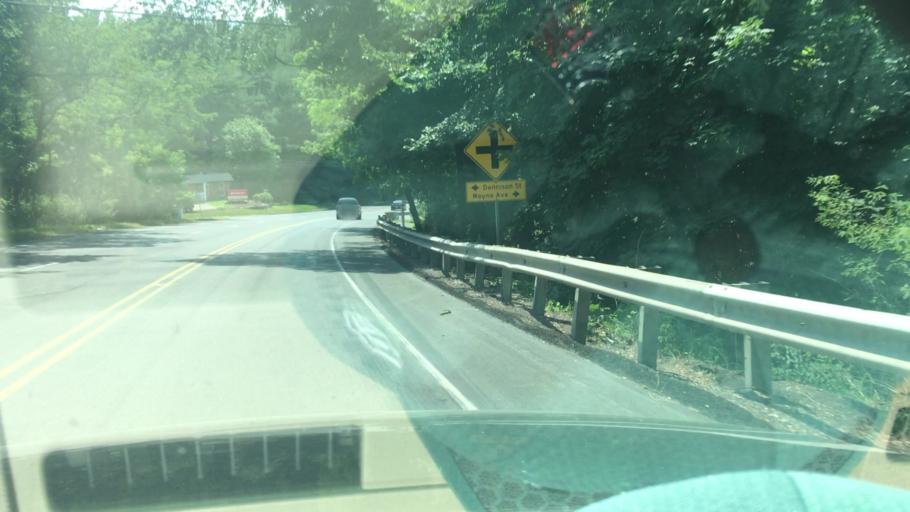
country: US
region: Pennsylvania
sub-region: Schuylkill County
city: Hometown
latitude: 40.8216
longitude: -75.9791
